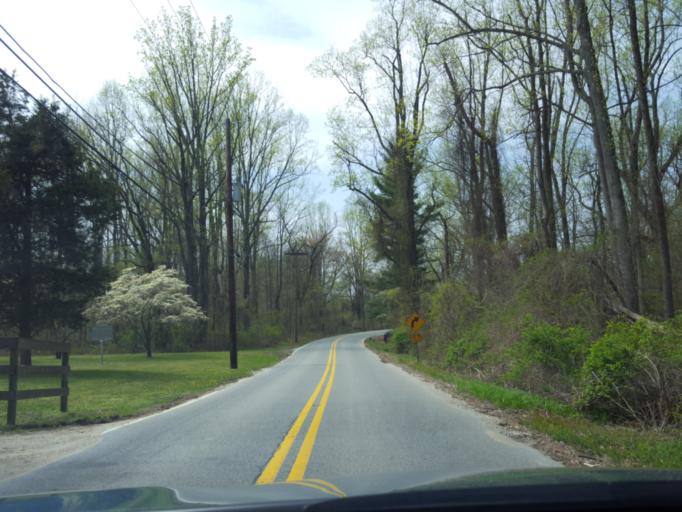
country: US
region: Maryland
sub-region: Prince George's County
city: Croom
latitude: 38.7478
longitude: -76.7561
